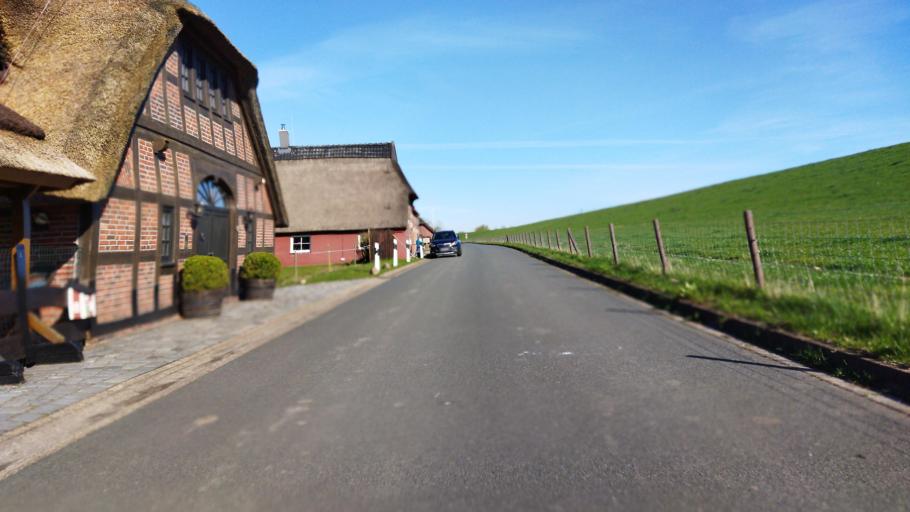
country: DE
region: Lower Saxony
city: Elsfleth
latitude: 53.2085
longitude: 8.4850
